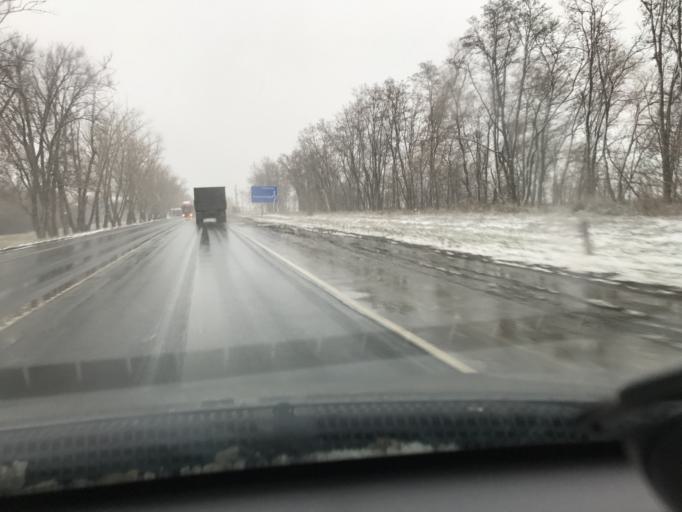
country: RU
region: Rostov
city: Yegorlykskaya
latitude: 46.5902
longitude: 40.6291
